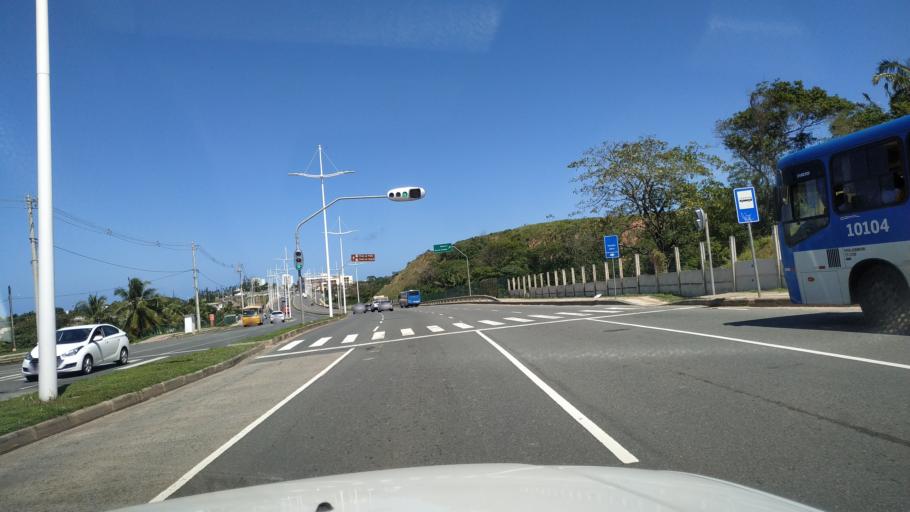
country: BR
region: Bahia
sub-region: Lauro De Freitas
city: Lauro de Freitas
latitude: -12.9338
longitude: -38.3844
